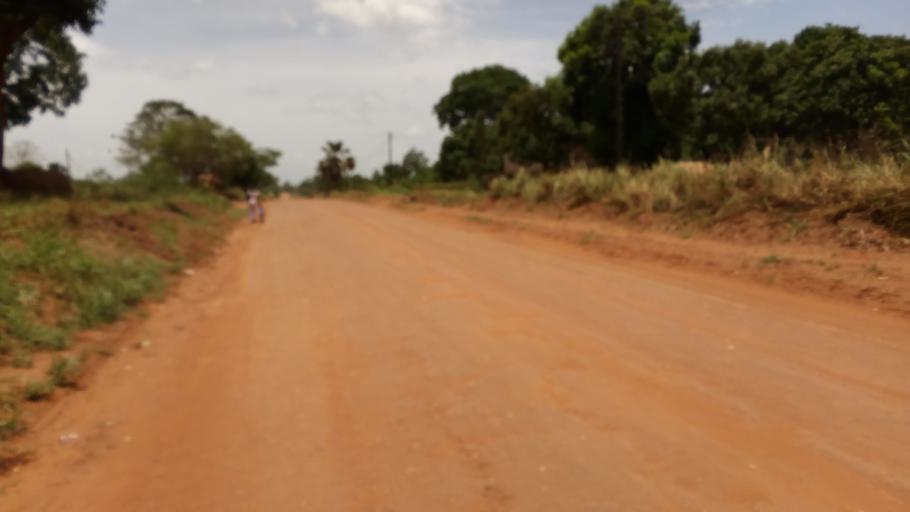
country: UG
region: Northern Region
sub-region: Gulu District
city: Gulu
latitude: 2.8023
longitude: 32.3194
